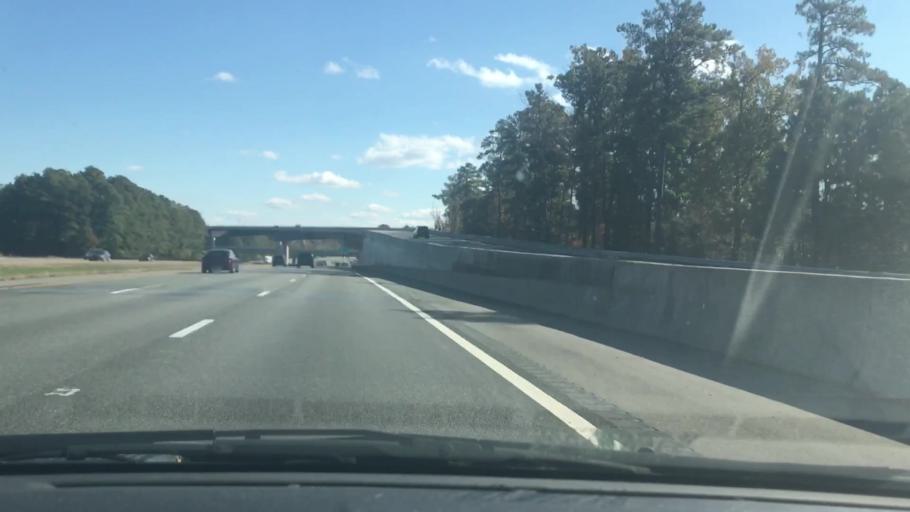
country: US
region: Virginia
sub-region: Henrico County
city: Short Pump
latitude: 37.6568
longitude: -77.6103
